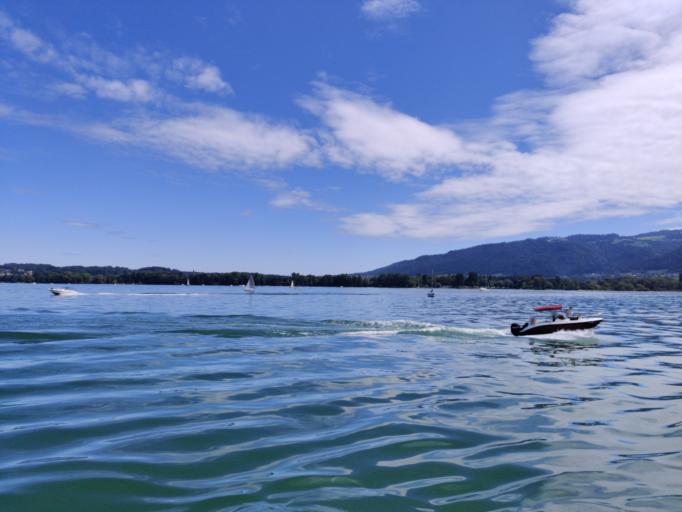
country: AT
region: Vorarlberg
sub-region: Politischer Bezirk Bregenz
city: Lochau
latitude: 47.5306
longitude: 9.7165
